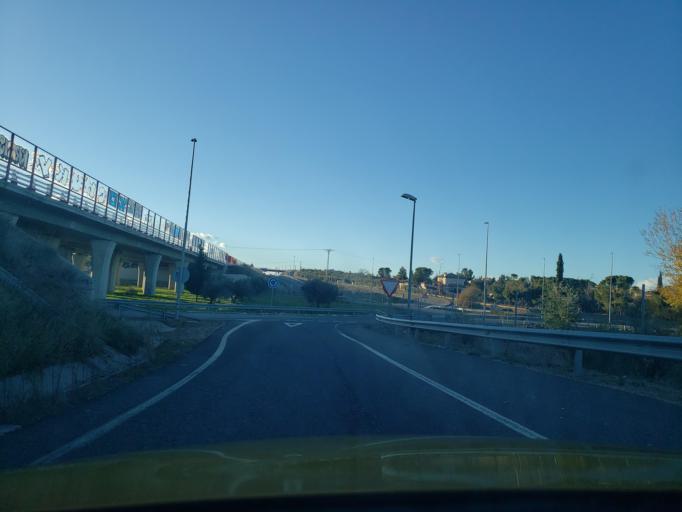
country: ES
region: Castille-La Mancha
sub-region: Province of Toledo
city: Cobisa
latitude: 39.8148
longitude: -4.0226
